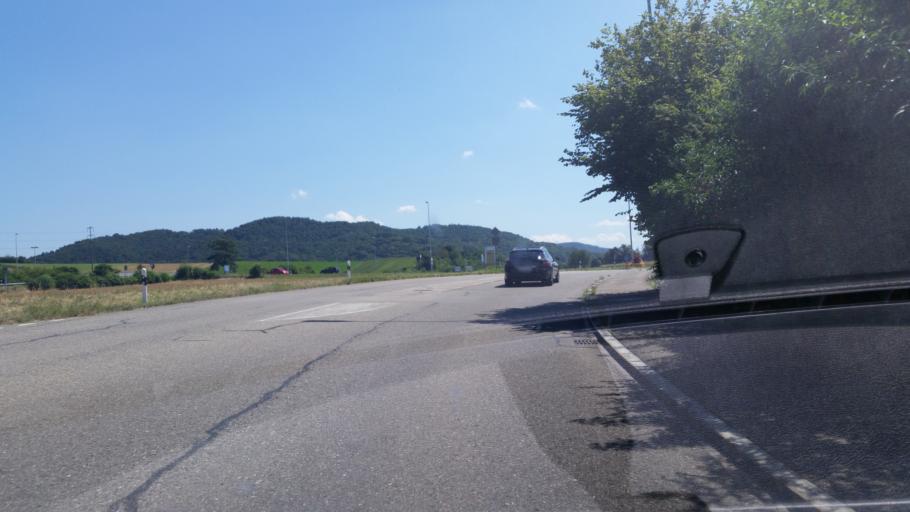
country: CH
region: Zurich
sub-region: Bezirk Buelach
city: Glattfelden
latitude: 47.5575
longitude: 8.5112
